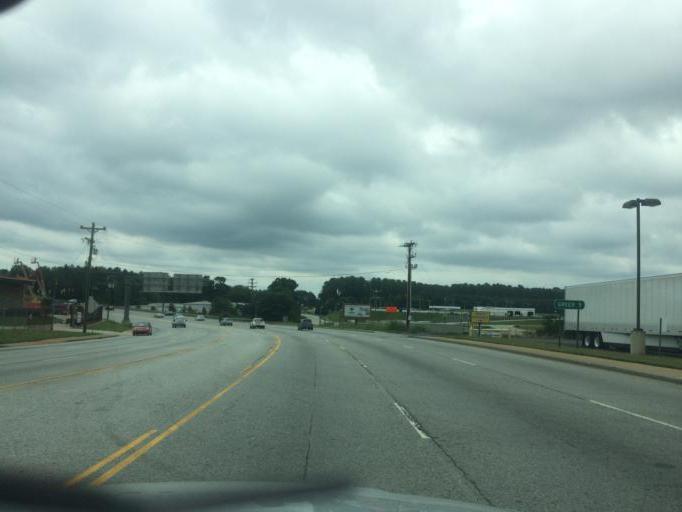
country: US
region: South Carolina
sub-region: Greenville County
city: Greer
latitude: 34.8743
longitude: -82.2250
